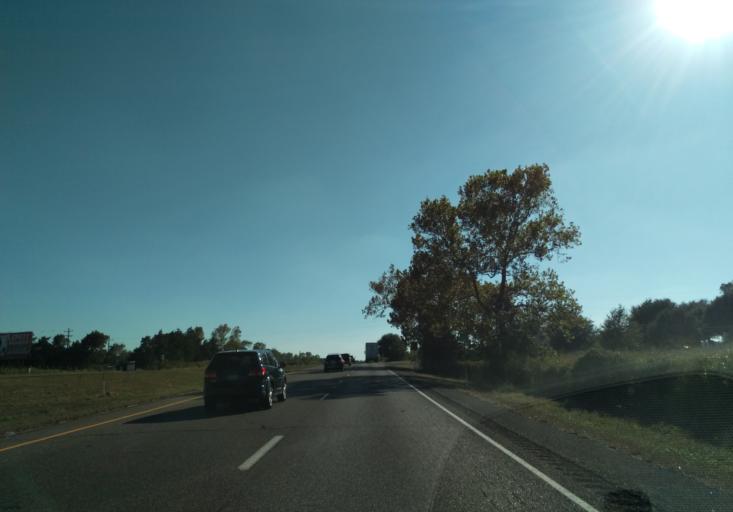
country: US
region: Texas
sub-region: Grimes County
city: Navasota
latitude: 30.2574
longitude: -96.0440
